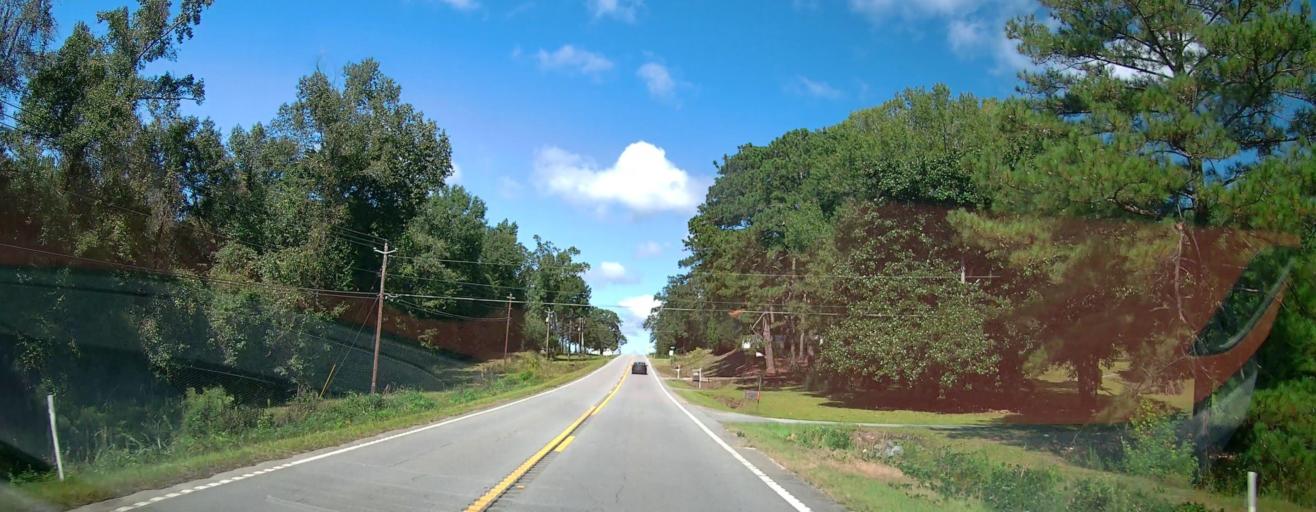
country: US
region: Georgia
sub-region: Bibb County
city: Macon
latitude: 32.8188
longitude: -83.5699
